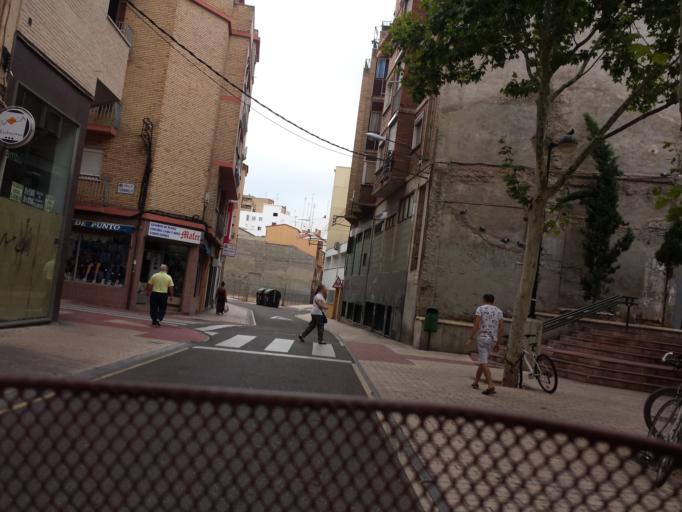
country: ES
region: Aragon
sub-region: Provincia de Zaragoza
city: Delicias
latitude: 41.6527
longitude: -0.9072
